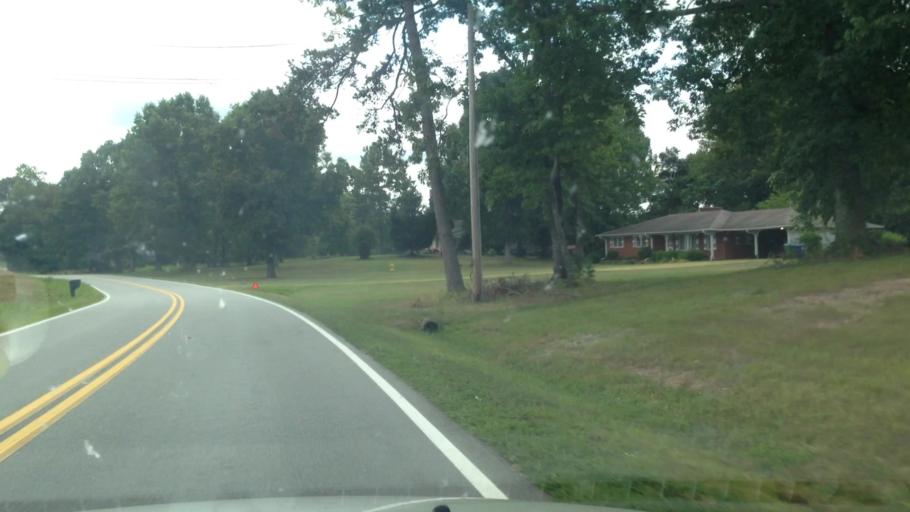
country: US
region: North Carolina
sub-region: Rockingham County
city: Mayodan
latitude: 36.3968
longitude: -80.0286
